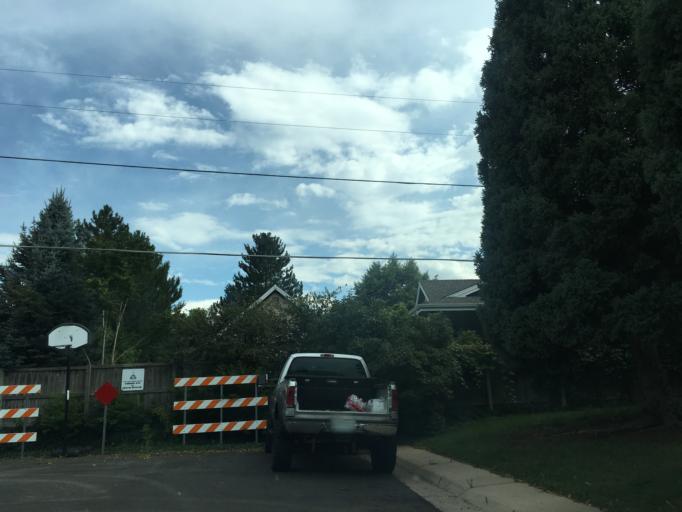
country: US
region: Colorado
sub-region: Jefferson County
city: Lakewood
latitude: 39.6752
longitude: -105.0622
